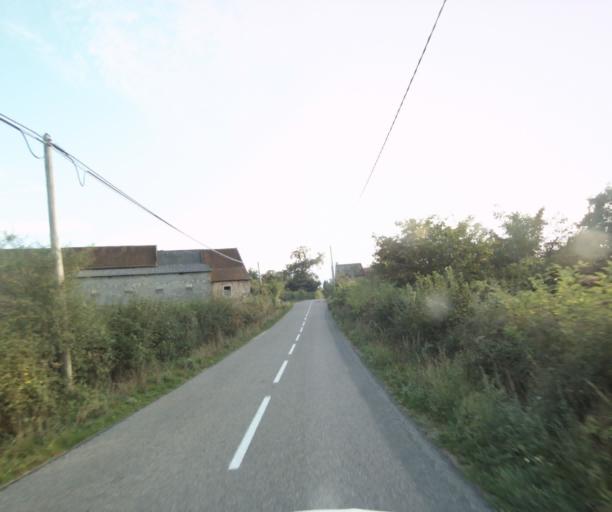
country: FR
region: Bourgogne
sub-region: Departement de Saone-et-Loire
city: Charolles
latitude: 46.4093
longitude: 4.4024
